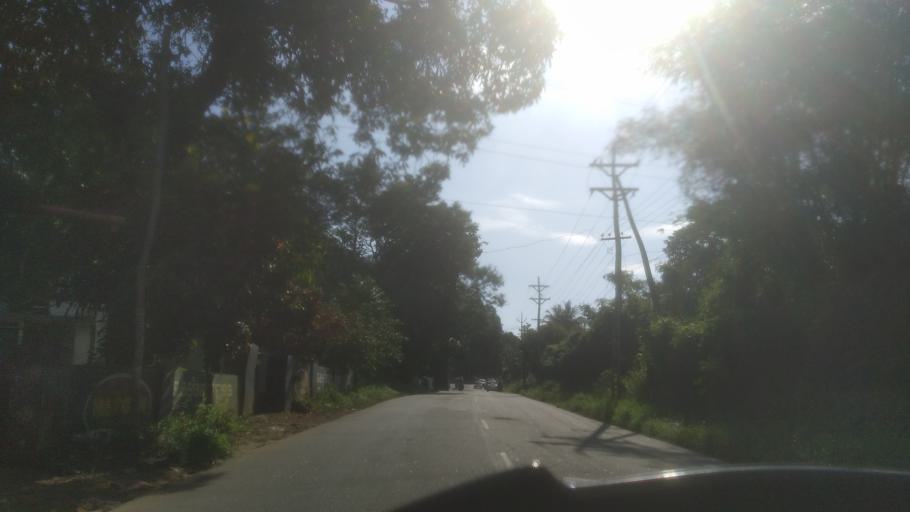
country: IN
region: Kerala
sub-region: Ernakulam
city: Muvattupuzha
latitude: 9.9832
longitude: 76.5595
